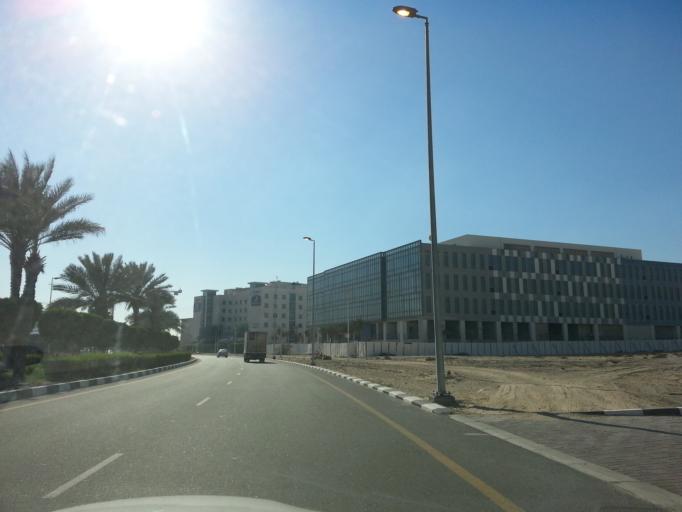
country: AE
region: Dubai
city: Dubai
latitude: 25.0091
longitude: 55.1588
